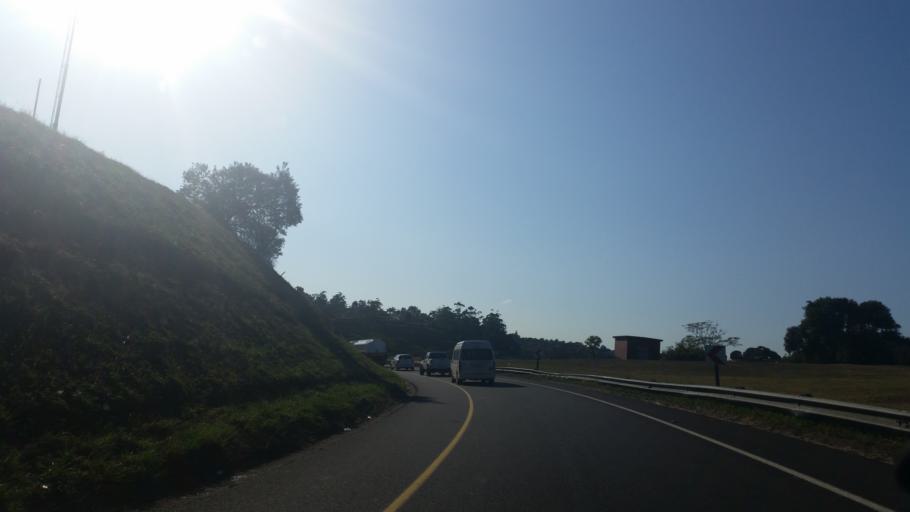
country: ZA
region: KwaZulu-Natal
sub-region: eThekwini Metropolitan Municipality
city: Berea
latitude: -29.8402
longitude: 30.9558
